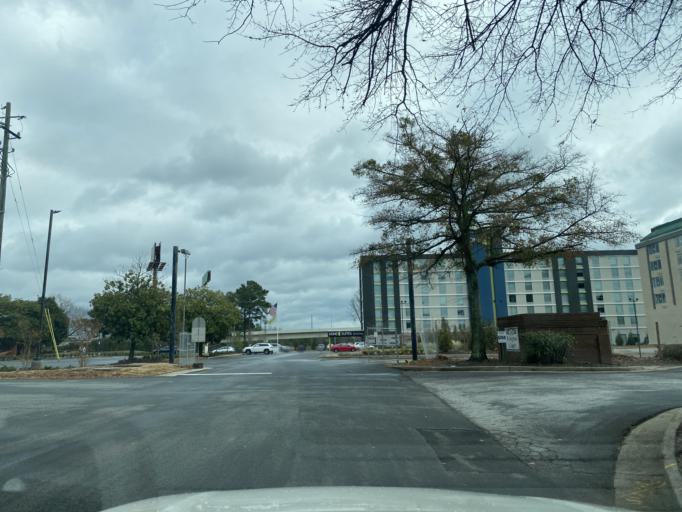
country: US
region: Georgia
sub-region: Cobb County
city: Smyrna
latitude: 33.9240
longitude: -84.4889
